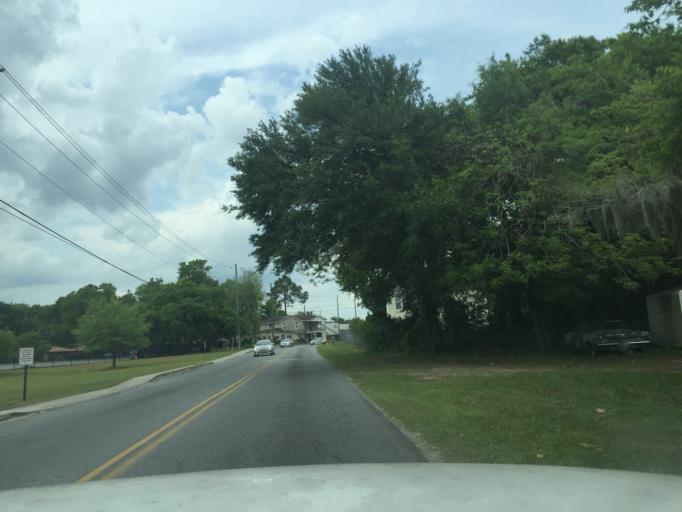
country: US
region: Georgia
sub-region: Chatham County
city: Thunderbolt
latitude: 32.0323
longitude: -81.0573
